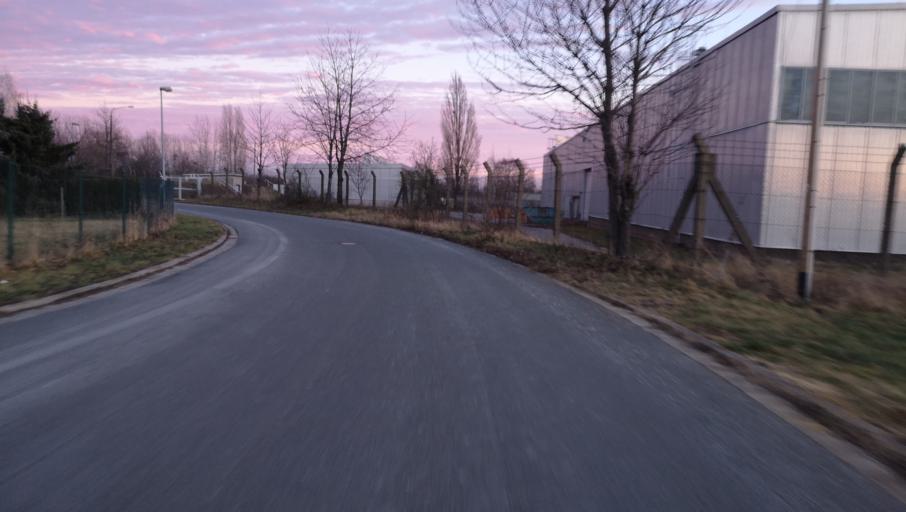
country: DE
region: Thuringia
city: Ronneburg
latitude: 50.8679
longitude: 12.1707
